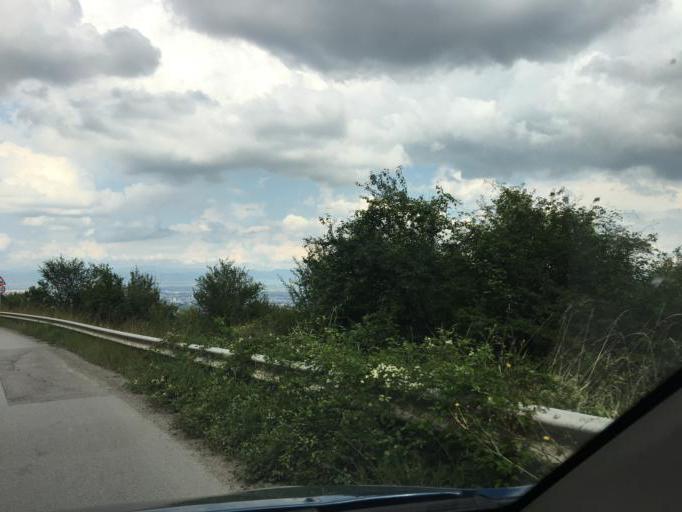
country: BG
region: Sofia-Capital
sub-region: Stolichna Obshtina
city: Sofia
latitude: 42.5927
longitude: 23.3668
